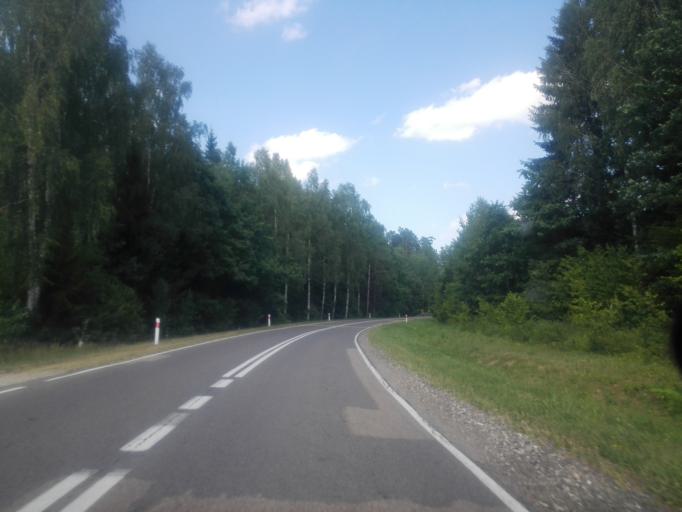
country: PL
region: Podlasie
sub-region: Powiat sejnenski
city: Sejny
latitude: 54.0094
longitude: 23.3252
